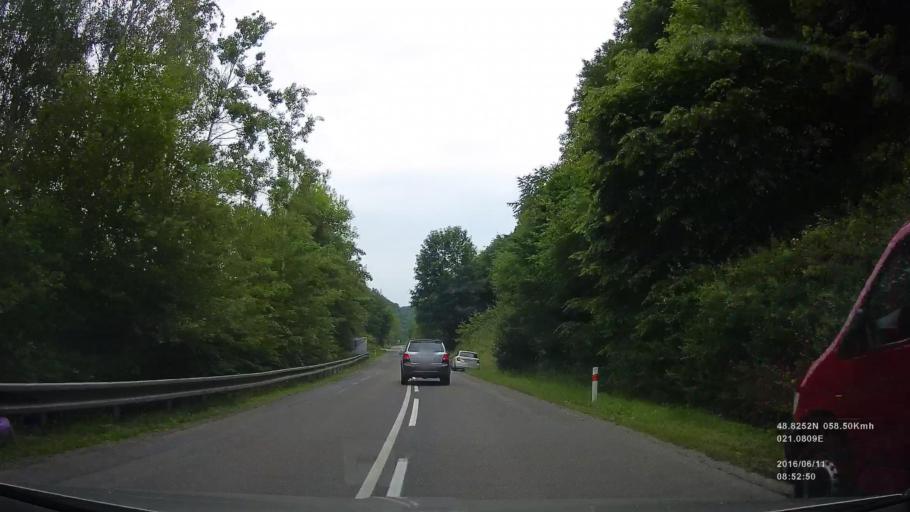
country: SK
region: Kosicky
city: Gelnica
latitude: 48.8202
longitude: 21.0824
